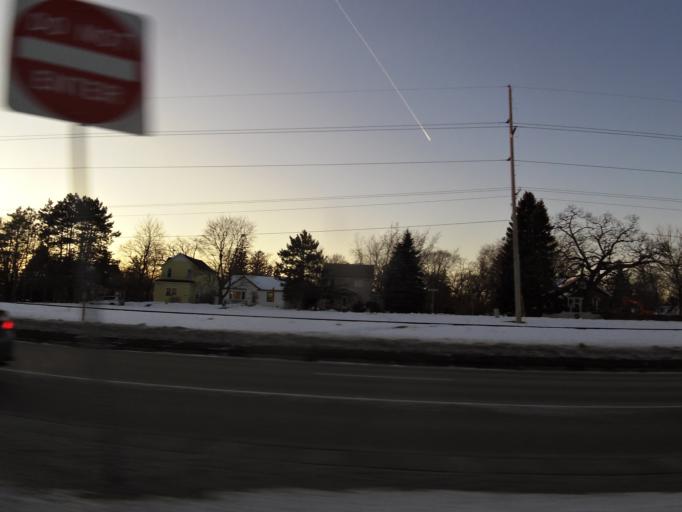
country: US
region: Minnesota
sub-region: Ramsey County
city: White Bear Lake
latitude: 45.0758
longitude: -93.0181
